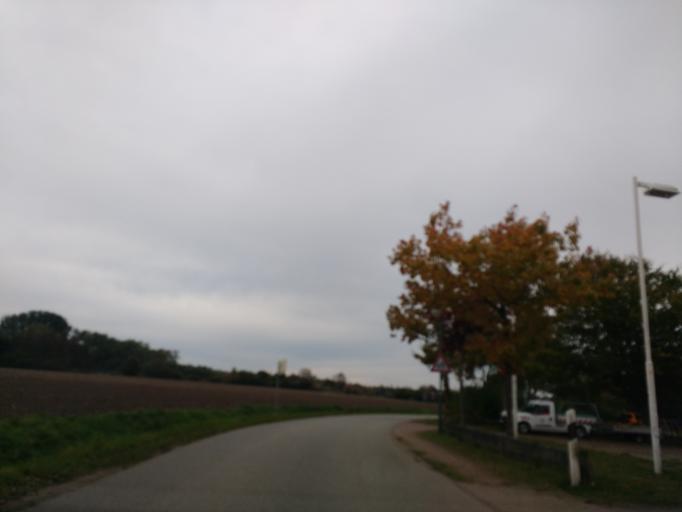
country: DE
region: Schleswig-Holstein
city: Grube
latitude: 54.2027
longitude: 11.0215
